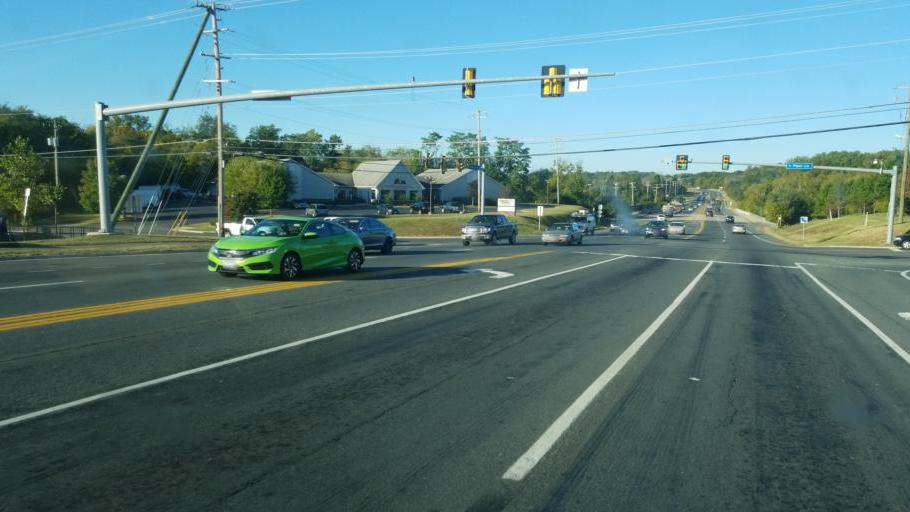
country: US
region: Virginia
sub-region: Prince William County
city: Bull Run
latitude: 38.7378
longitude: -77.5324
